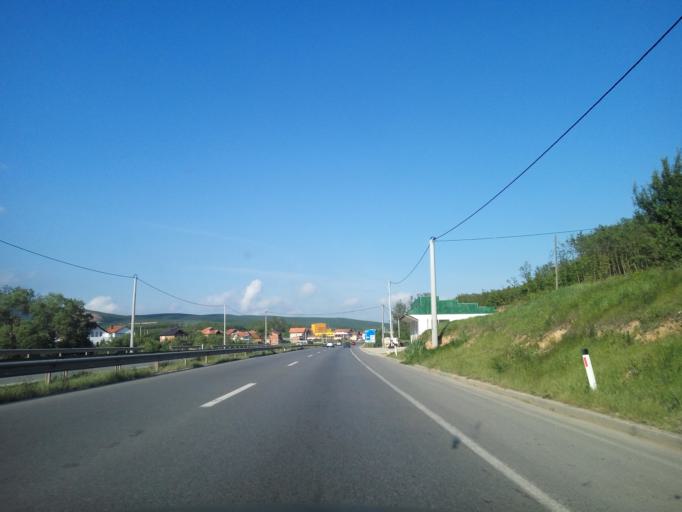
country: XK
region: Pristina
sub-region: Komuna e Drenasit
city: Glogovac
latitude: 42.6011
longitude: 20.9413
